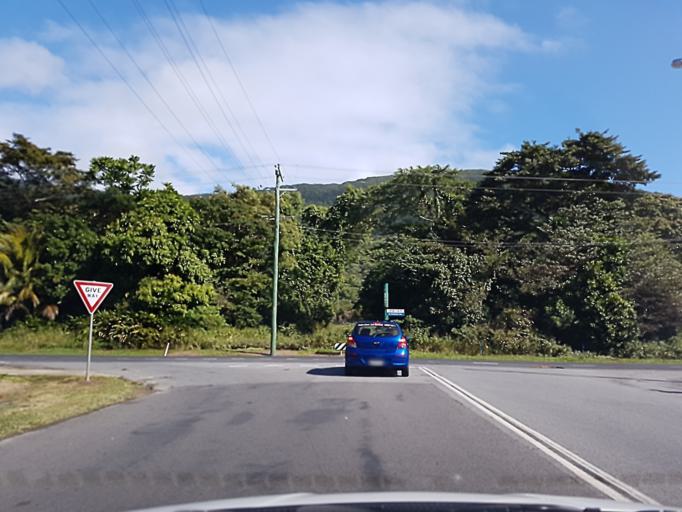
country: AU
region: Queensland
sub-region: Cairns
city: Palm Cove
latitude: -16.7480
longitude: 145.6631
